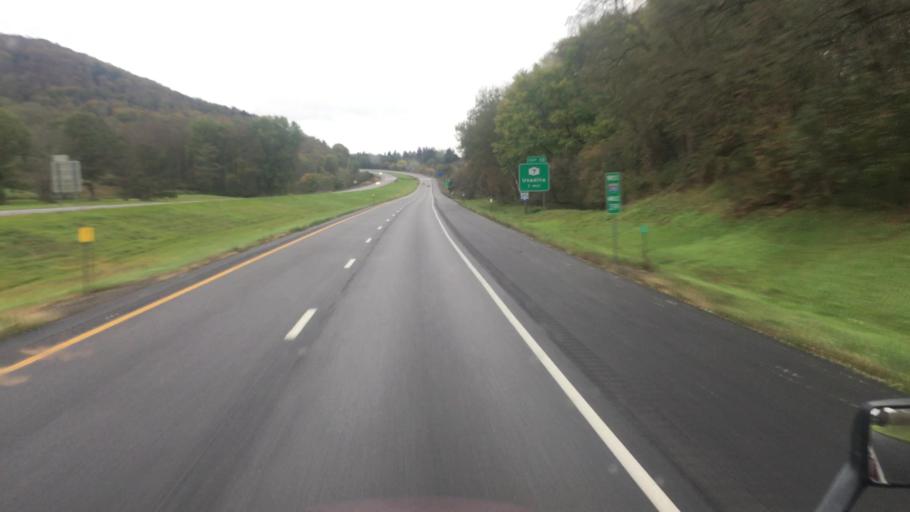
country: US
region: New York
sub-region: Otsego County
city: Unadilla
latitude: 42.3238
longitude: -75.2999
